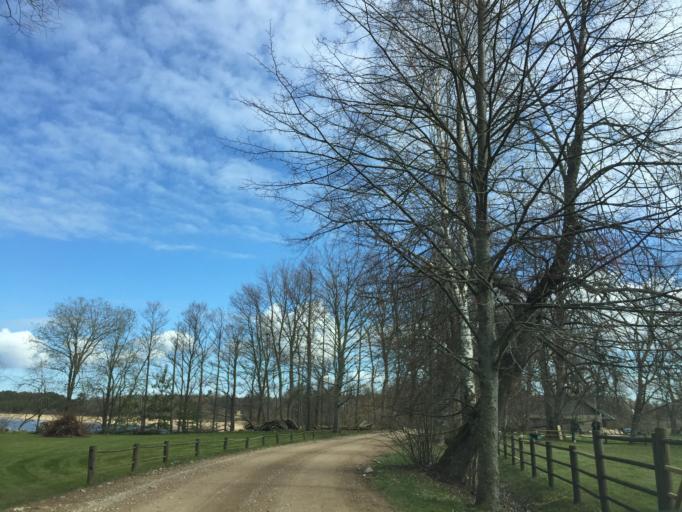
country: LV
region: Salacgrivas
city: Salacgriva
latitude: 57.6099
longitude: 24.3832
